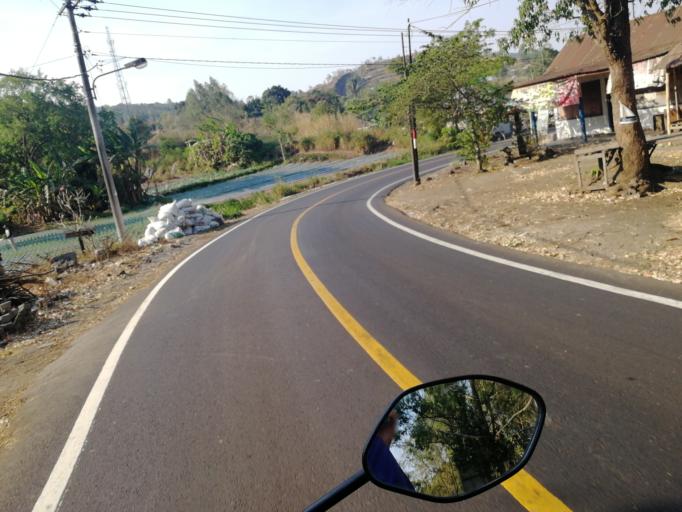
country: ID
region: Bali
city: Banjar Trunyan
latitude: -8.2515
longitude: 115.3964
